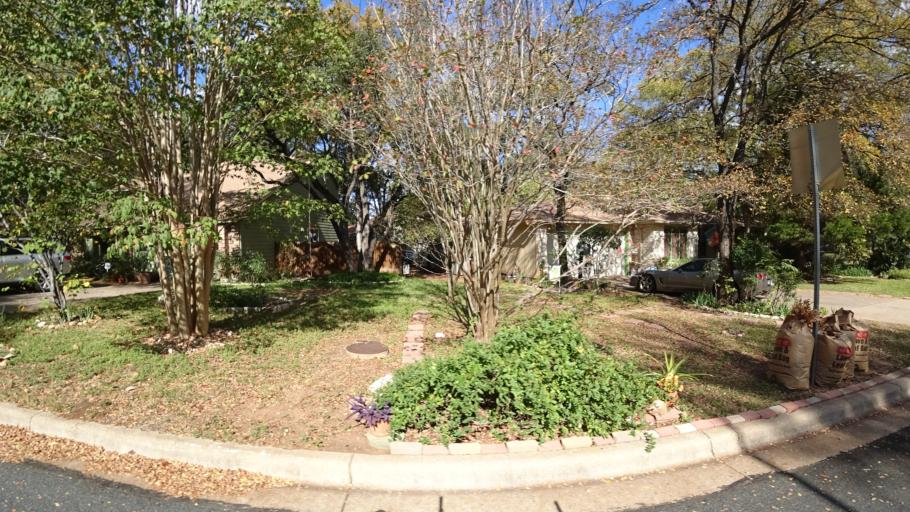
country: US
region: Texas
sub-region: Travis County
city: Wells Branch
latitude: 30.4206
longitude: -97.7244
